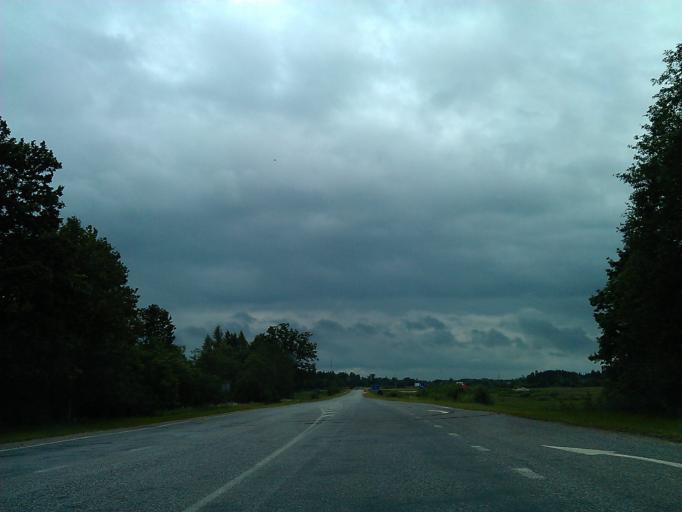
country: LV
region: Kuldigas Rajons
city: Kuldiga
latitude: 56.9789
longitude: 22.0165
